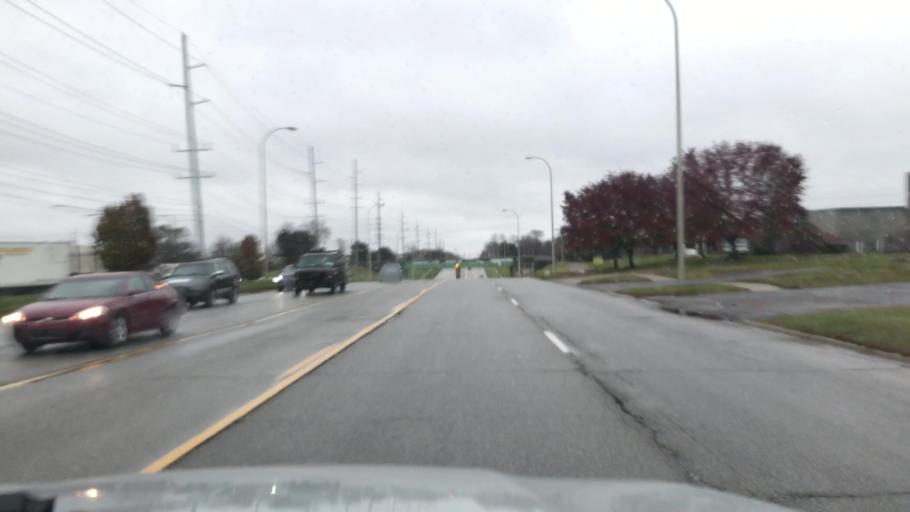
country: US
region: Michigan
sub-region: Wayne County
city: Westland
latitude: 42.3794
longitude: -83.4120
